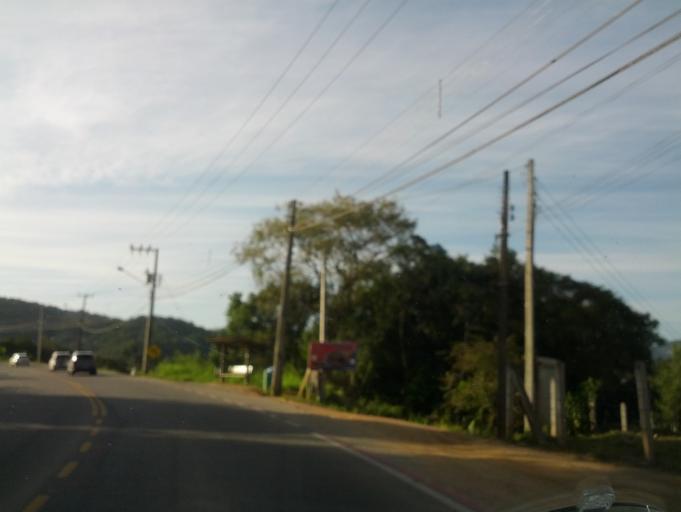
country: BR
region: Santa Catarina
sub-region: Indaial
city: Indaial
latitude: -26.8885
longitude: -49.1625
